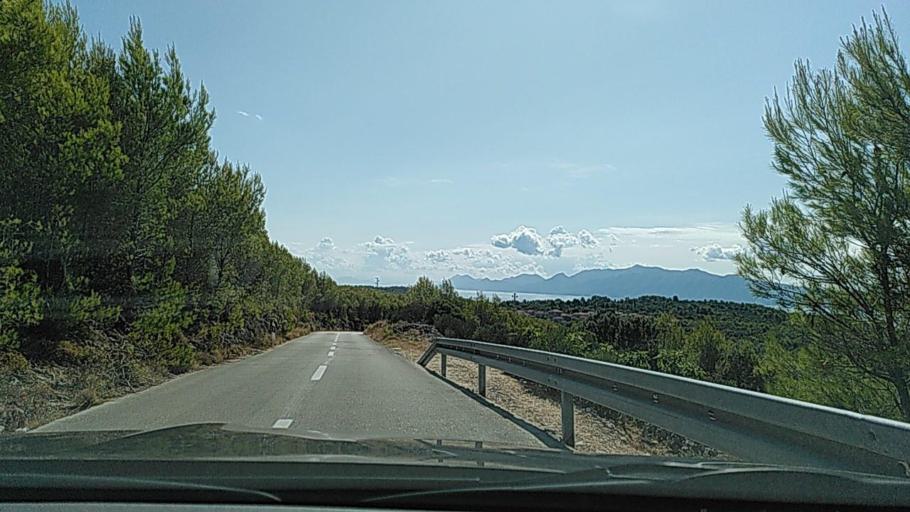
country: HR
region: Splitsko-Dalmatinska
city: Tucepi
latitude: 43.1338
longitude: 16.9767
